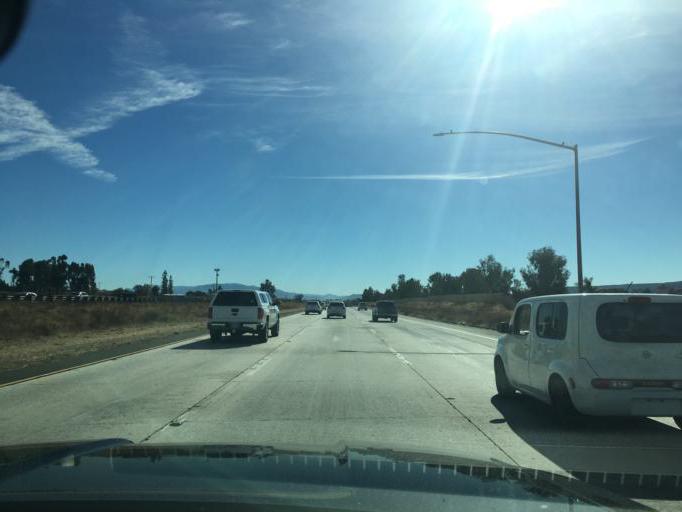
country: US
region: California
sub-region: Riverside County
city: Wildomar
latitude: 33.6091
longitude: -117.2574
